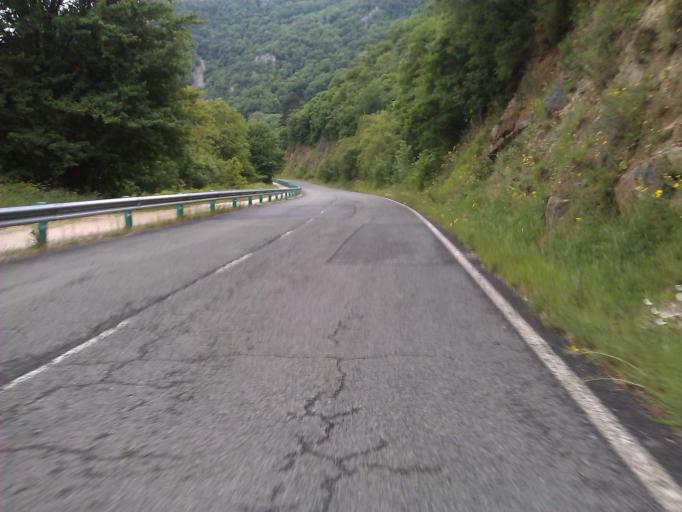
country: ES
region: Navarre
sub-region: Provincia de Navarra
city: Irurtzun
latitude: 42.9499
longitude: -1.8273
